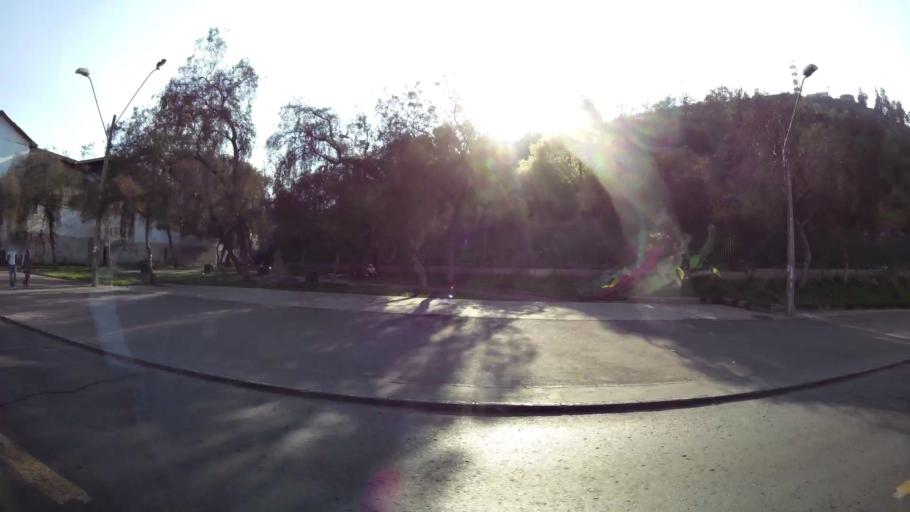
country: CL
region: Santiago Metropolitan
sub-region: Provincia de Santiago
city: Santiago
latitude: -33.4214
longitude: -70.6447
